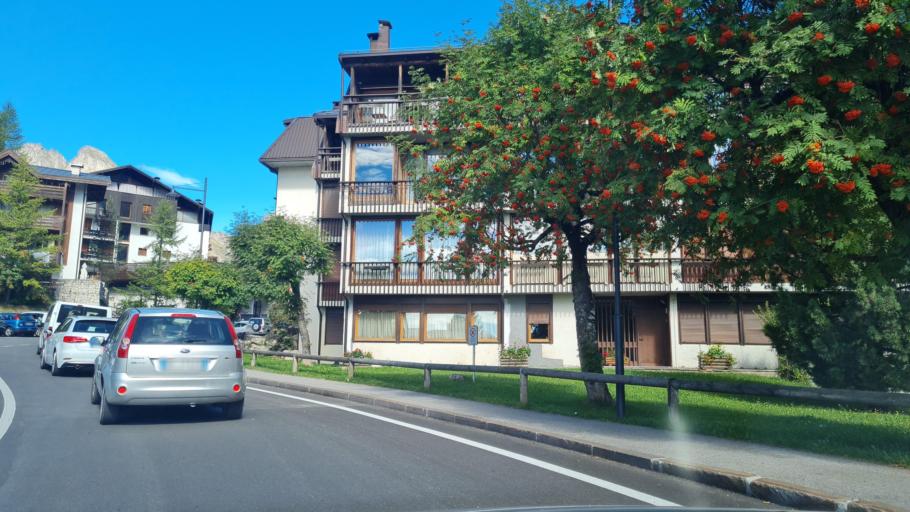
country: IT
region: Trentino-Alto Adige
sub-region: Provincia di Trento
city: Siror
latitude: 46.2600
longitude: 11.8017
